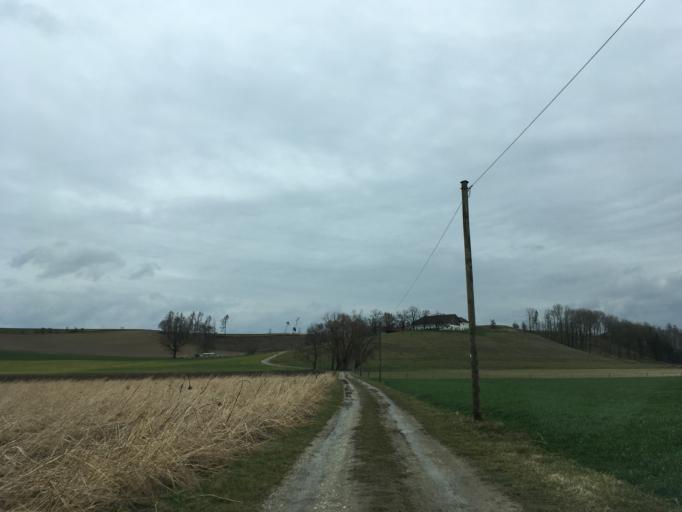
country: DE
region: Bavaria
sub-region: Upper Bavaria
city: Oberbergkirchen
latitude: 48.2594
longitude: 12.3624
